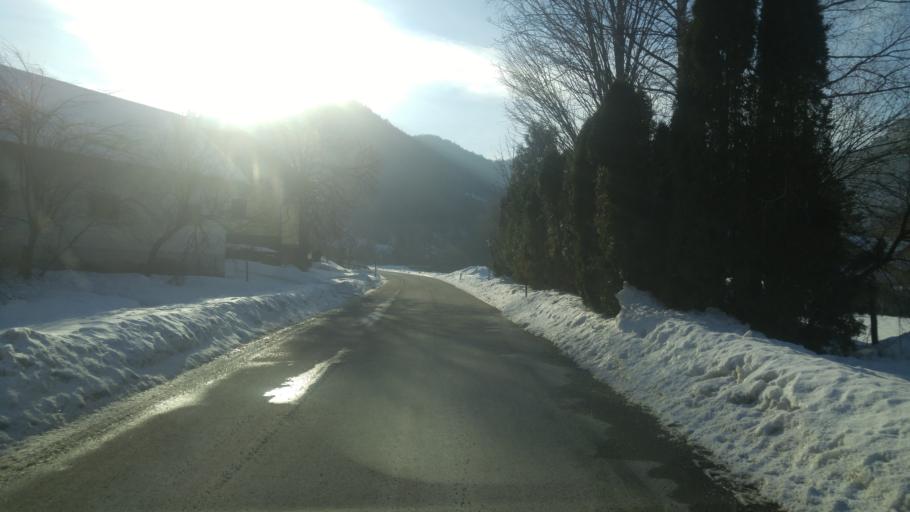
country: AT
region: Lower Austria
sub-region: Politischer Bezirk Lilienfeld
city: Hohenberg
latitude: 47.8968
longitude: 15.6201
